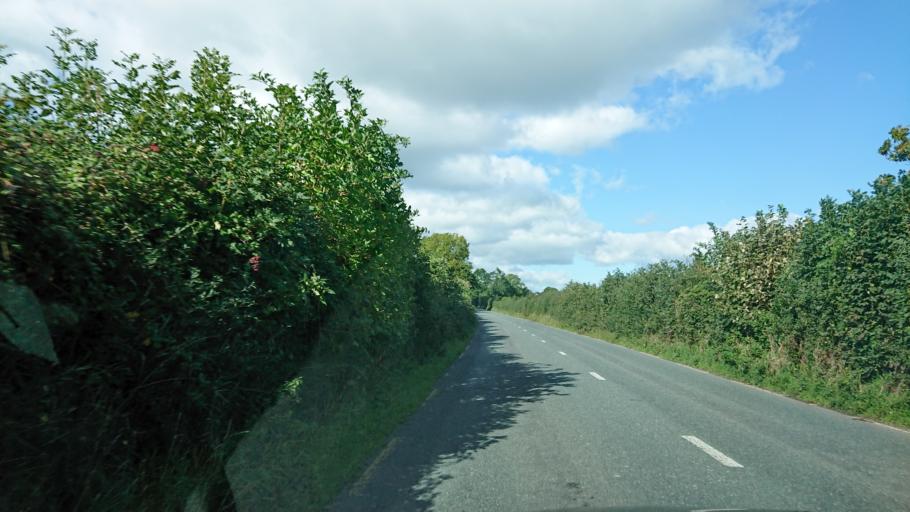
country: IE
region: Munster
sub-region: Waterford
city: Dungarvan
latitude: 52.1134
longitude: -7.6798
